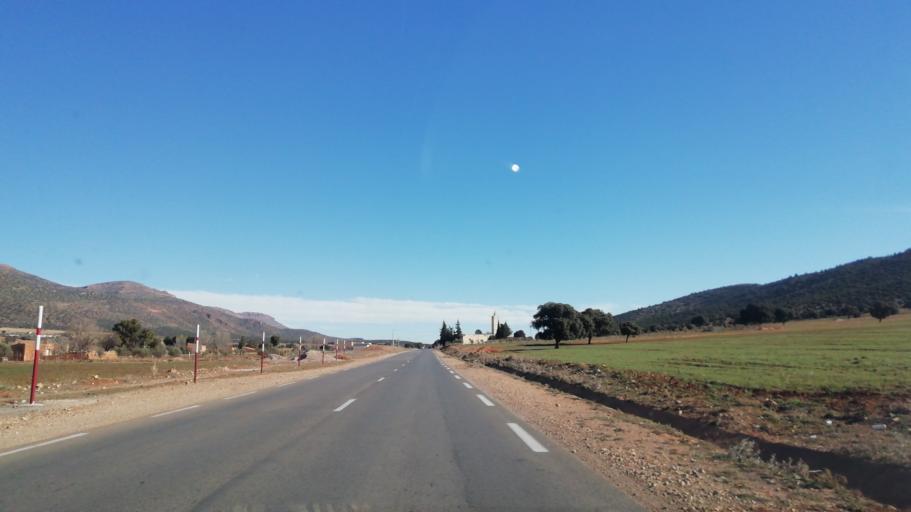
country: DZ
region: Tlemcen
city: Sebdou
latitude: 34.6883
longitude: -1.2457
